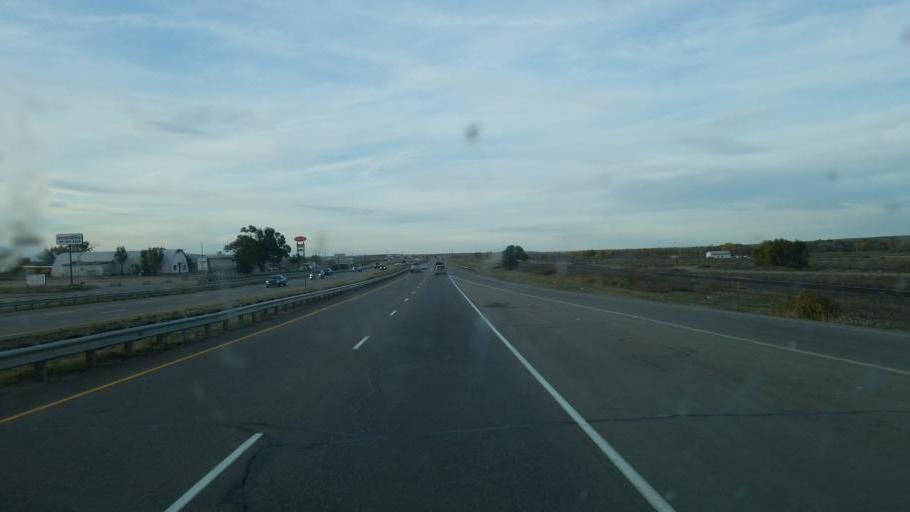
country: US
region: Colorado
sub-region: Pueblo County
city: Pueblo
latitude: 38.3452
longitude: -104.6197
